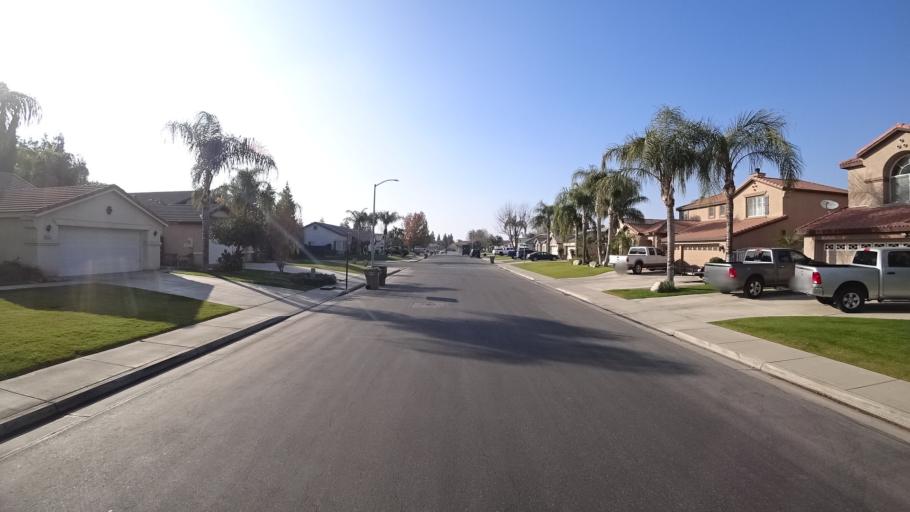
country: US
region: California
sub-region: Kern County
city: Greenacres
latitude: 35.4165
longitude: -119.0943
